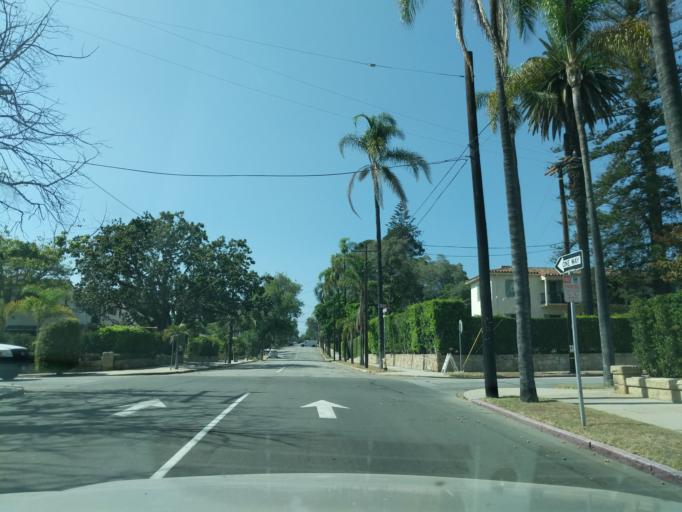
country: US
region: California
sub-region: Santa Barbara County
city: Santa Barbara
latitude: 34.4310
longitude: -119.7097
